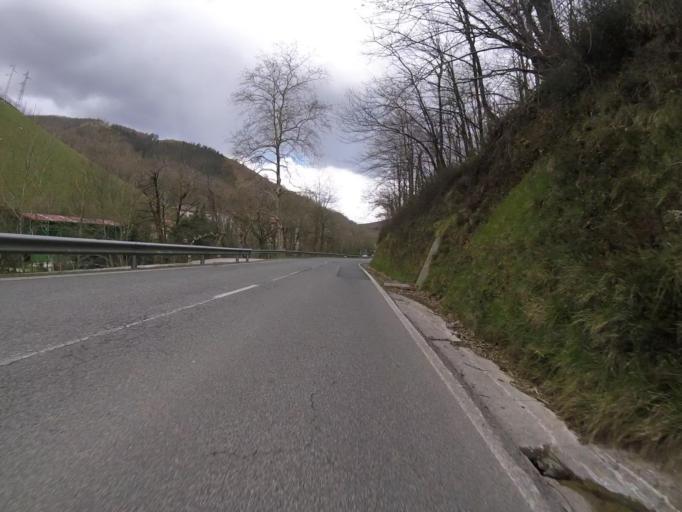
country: ES
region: Navarre
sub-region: Provincia de Navarra
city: Lesaka
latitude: 43.2410
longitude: -1.6695
